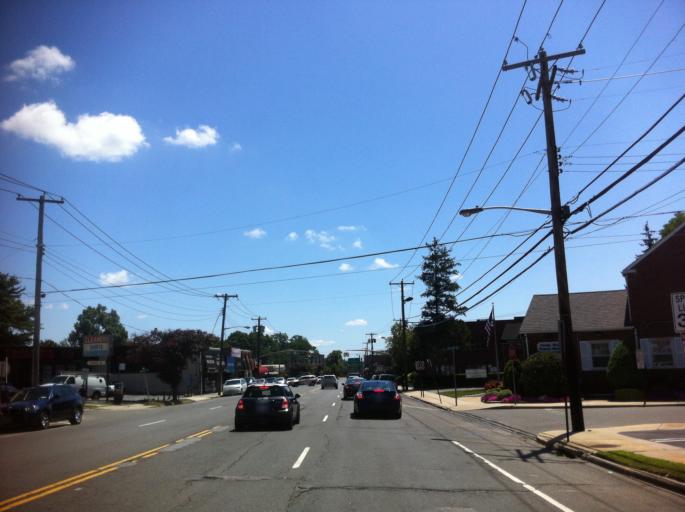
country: US
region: New York
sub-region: Nassau County
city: Roslyn Heights
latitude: 40.7905
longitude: -73.6529
